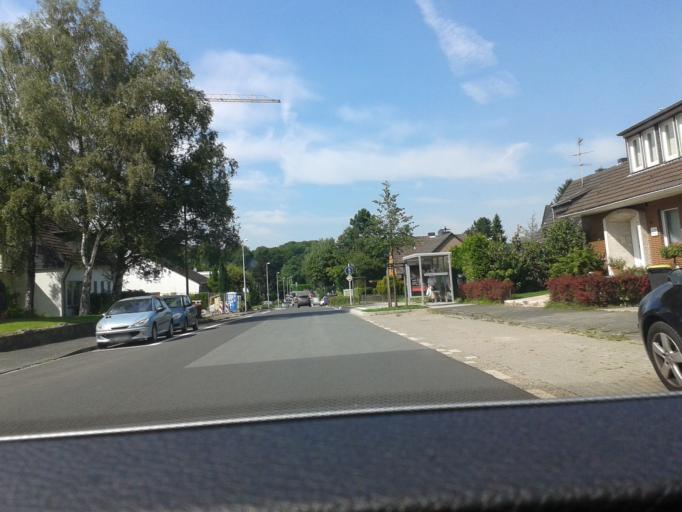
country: DE
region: North Rhine-Westphalia
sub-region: Regierungsbezirk Dusseldorf
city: Muelheim (Ruhr)
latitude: 51.3953
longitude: 6.8554
